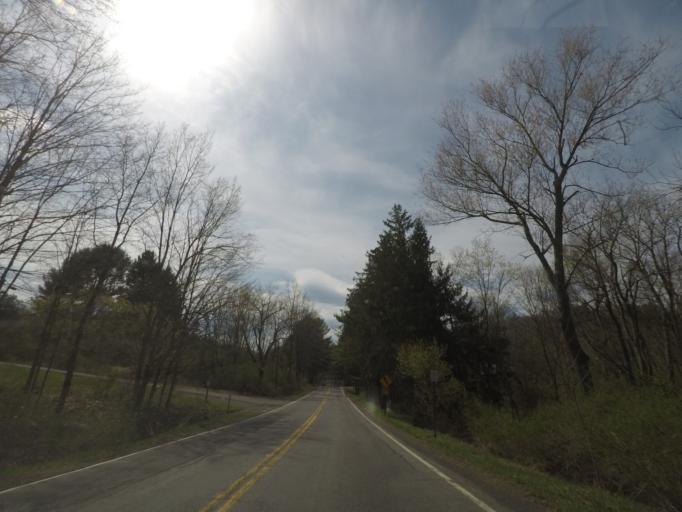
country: US
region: New York
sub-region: Columbia County
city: Chatham
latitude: 42.3452
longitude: -73.5846
